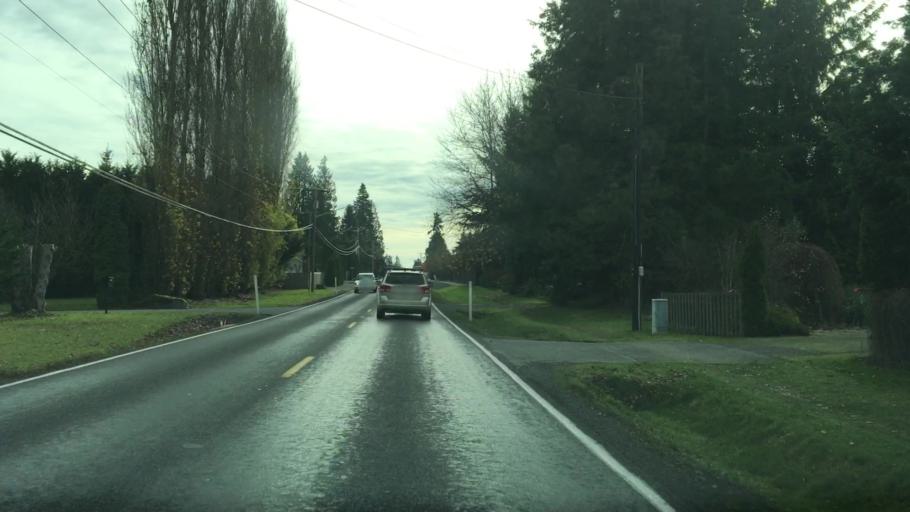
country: US
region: Washington
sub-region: Pierce County
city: South Hill
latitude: 47.1248
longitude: -122.3149
